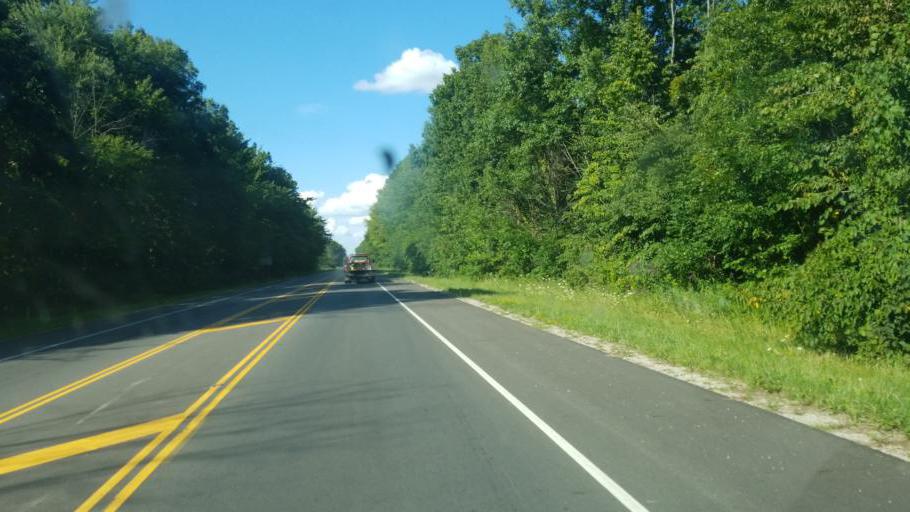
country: US
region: Ohio
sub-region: Franklin County
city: Westerville
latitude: 40.1820
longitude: -82.9119
